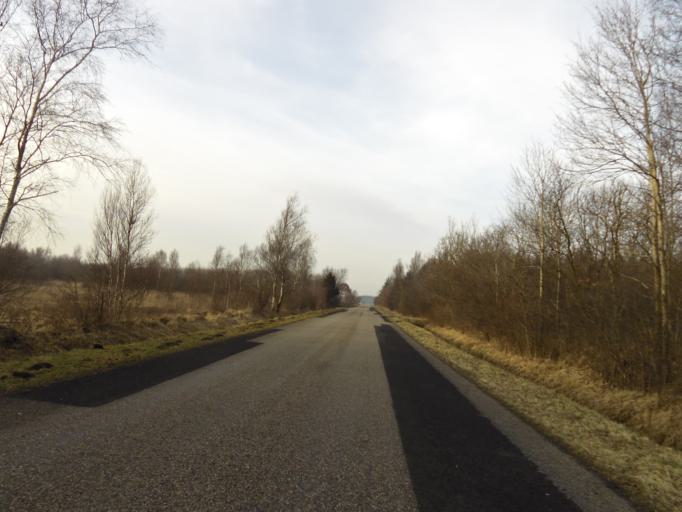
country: DK
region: South Denmark
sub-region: Tonder Kommune
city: Logumkloster
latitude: 55.1474
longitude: 8.8996
